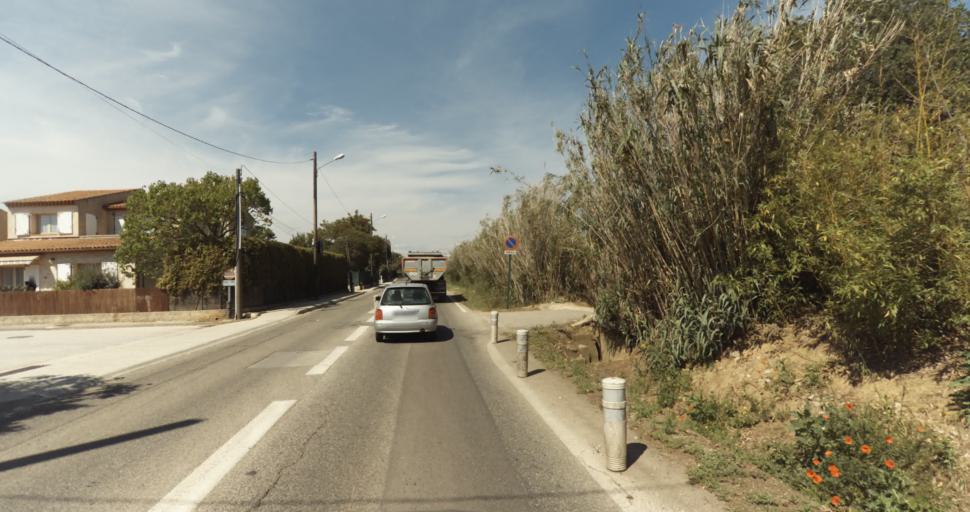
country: FR
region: Provence-Alpes-Cote d'Azur
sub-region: Departement du Var
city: Hyeres
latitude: 43.1265
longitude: 6.1548
